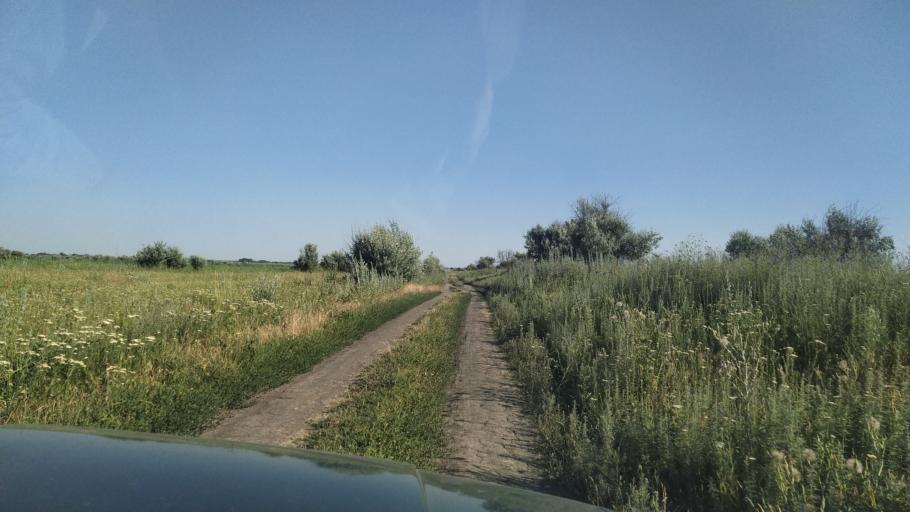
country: RU
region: Rostov
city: Kuleshovka
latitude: 47.1327
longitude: 39.6425
